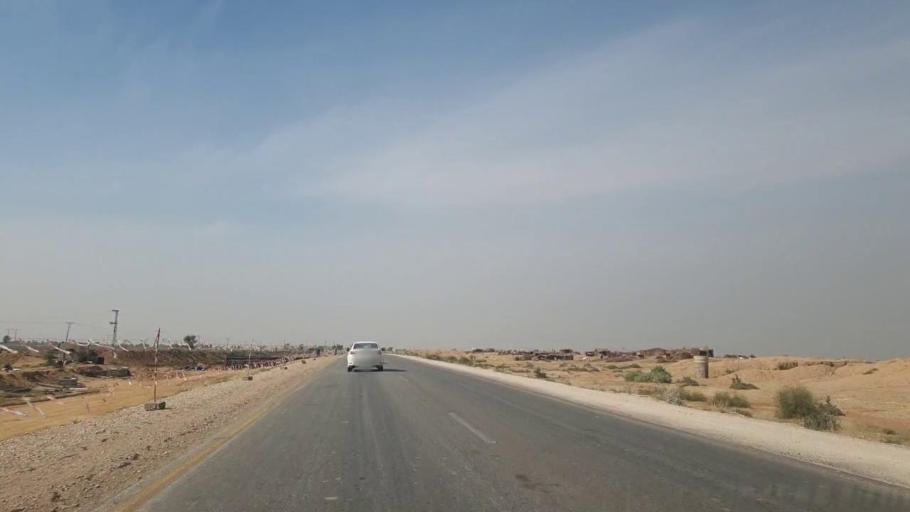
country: PK
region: Sindh
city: Sann
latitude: 26.0212
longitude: 68.1345
